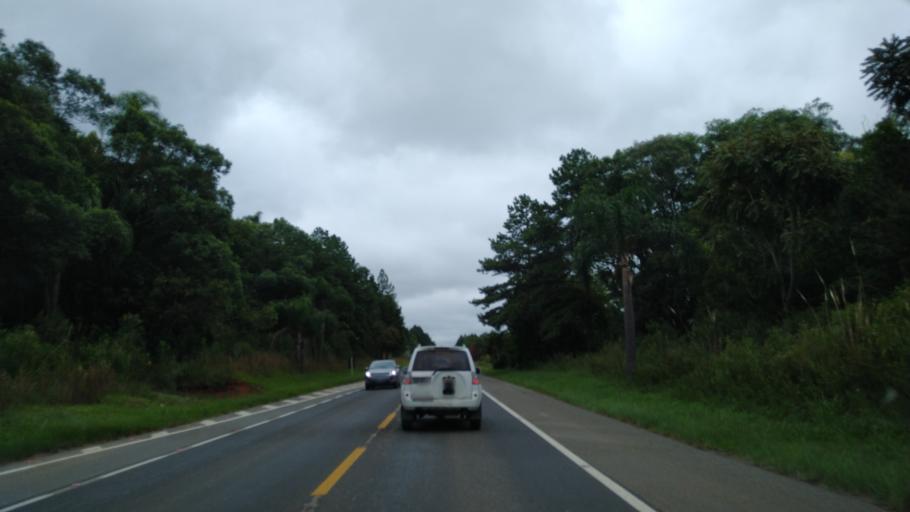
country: BR
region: Santa Catarina
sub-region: Tres Barras
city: Tres Barras
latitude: -26.1797
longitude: -50.1921
